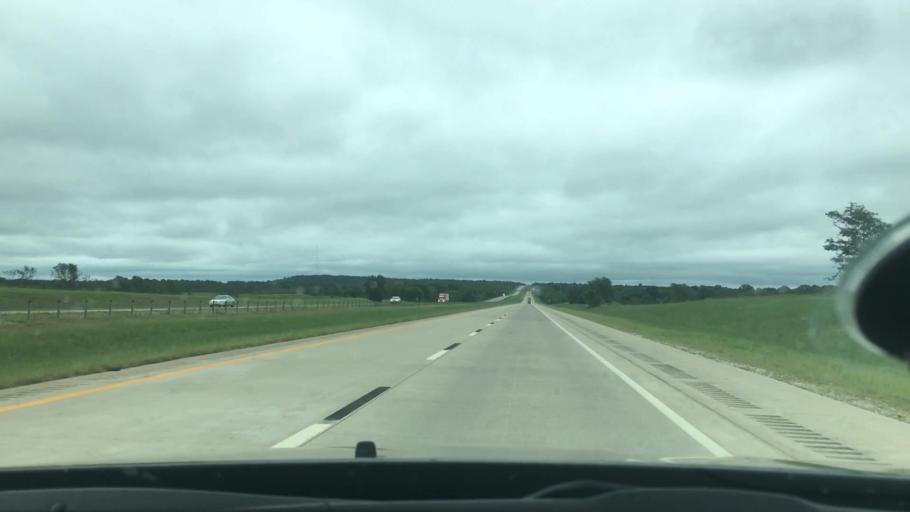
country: US
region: Oklahoma
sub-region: Muskogee County
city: Warner
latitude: 35.4822
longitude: -95.2661
